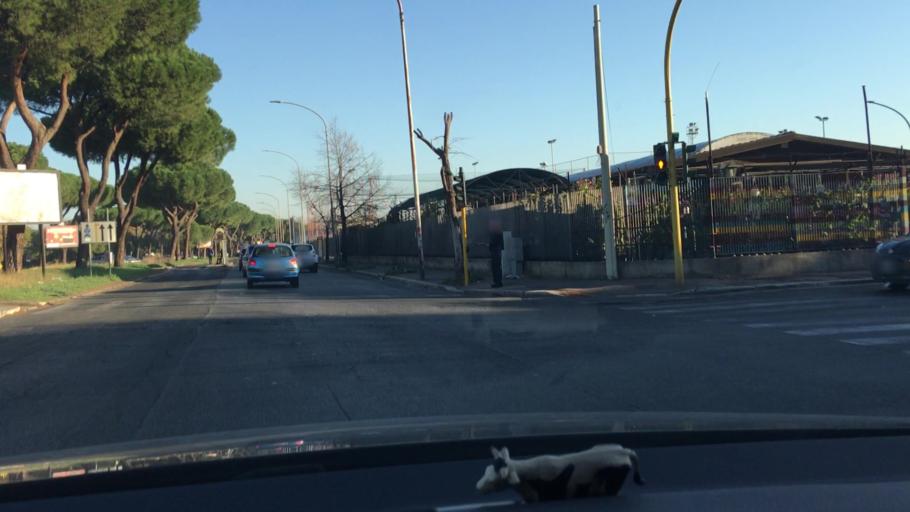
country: IT
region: Latium
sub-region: Citta metropolitana di Roma Capitale
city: Rome
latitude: 41.8697
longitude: 12.5683
